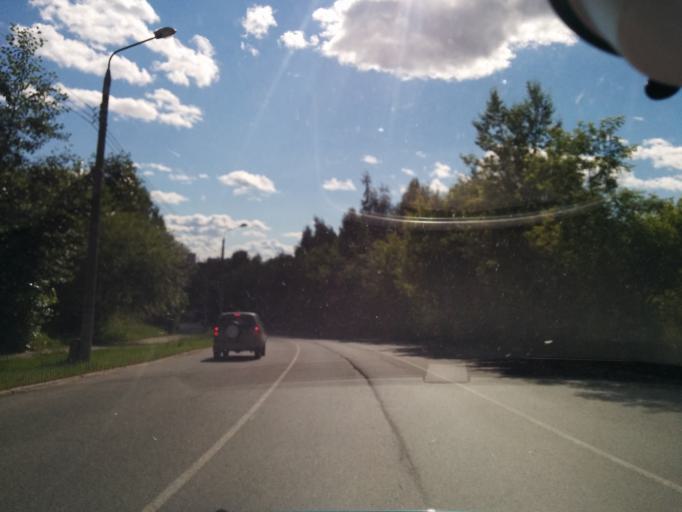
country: RU
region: Perm
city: Perm
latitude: 58.0104
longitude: 56.1972
